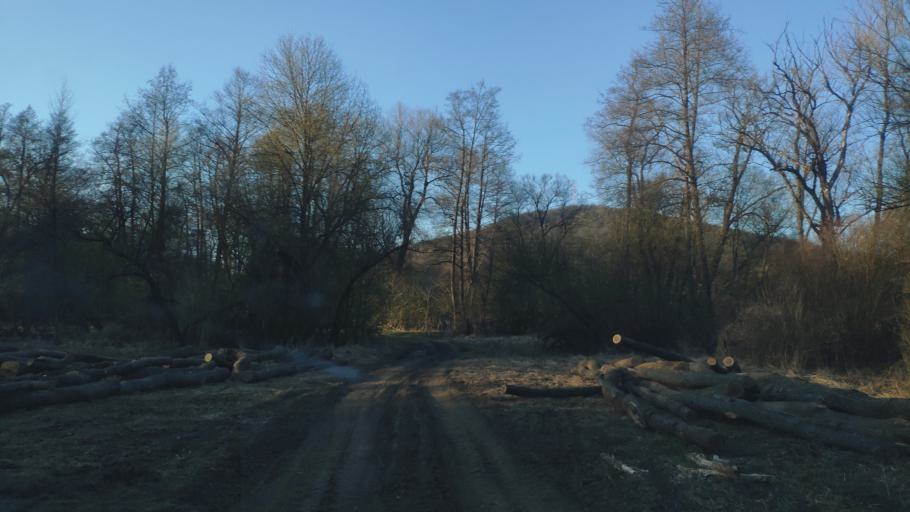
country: SK
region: Banskobystricky
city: Revuca
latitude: 48.5207
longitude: 20.3101
